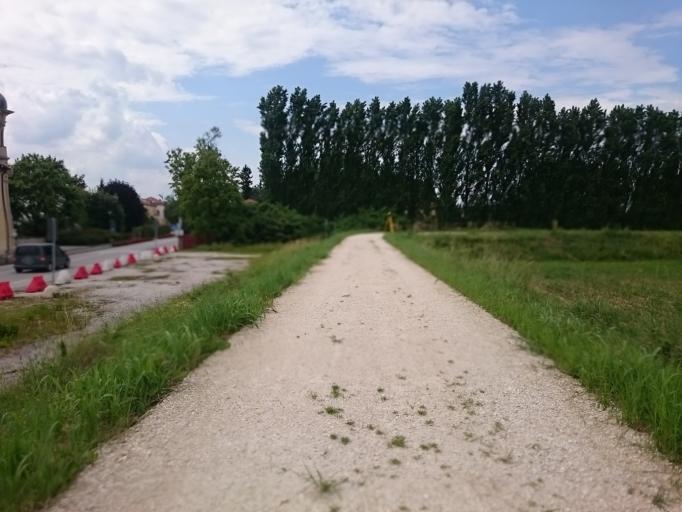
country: IT
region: Veneto
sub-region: Provincia di Vicenza
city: Montegaldella
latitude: 45.4353
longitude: 11.6753
